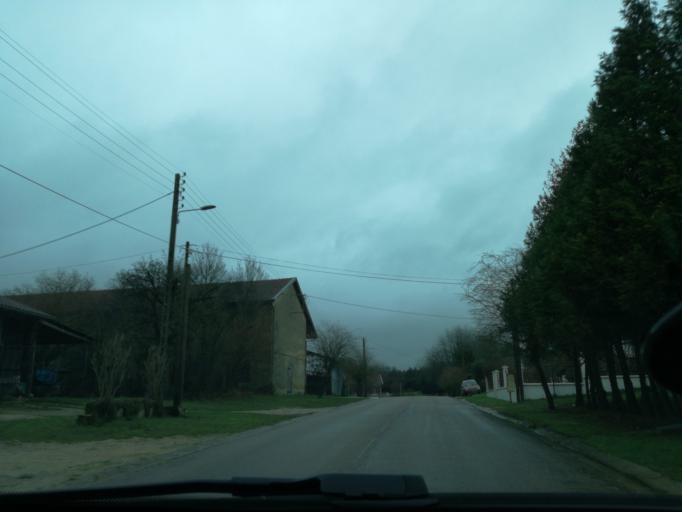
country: FR
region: Lorraine
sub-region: Departement de la Meuse
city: Clermont-en-Argonne
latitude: 48.9983
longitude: 5.0979
